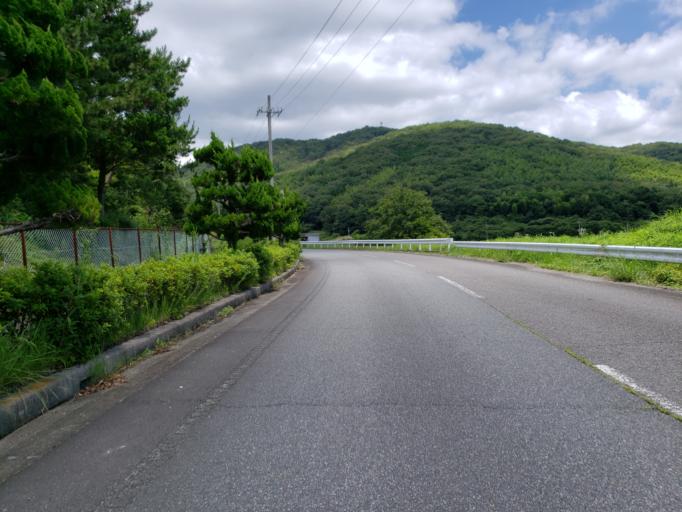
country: JP
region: Hyogo
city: Himeji
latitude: 34.8565
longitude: 134.7584
